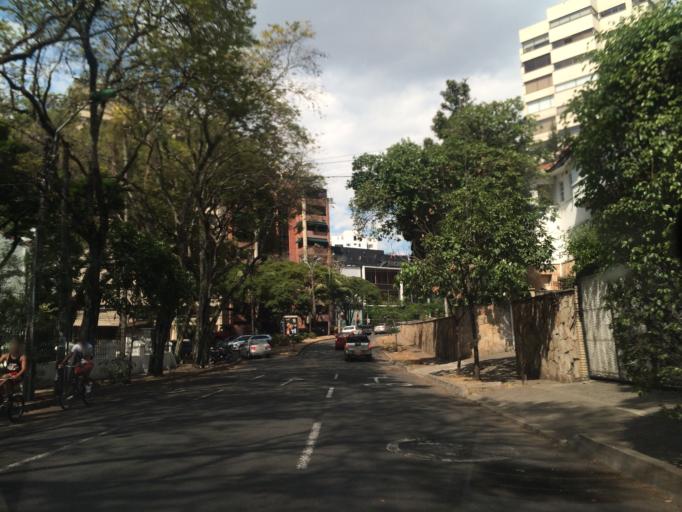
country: CO
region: Valle del Cauca
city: Cali
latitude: 3.4519
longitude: -76.5489
